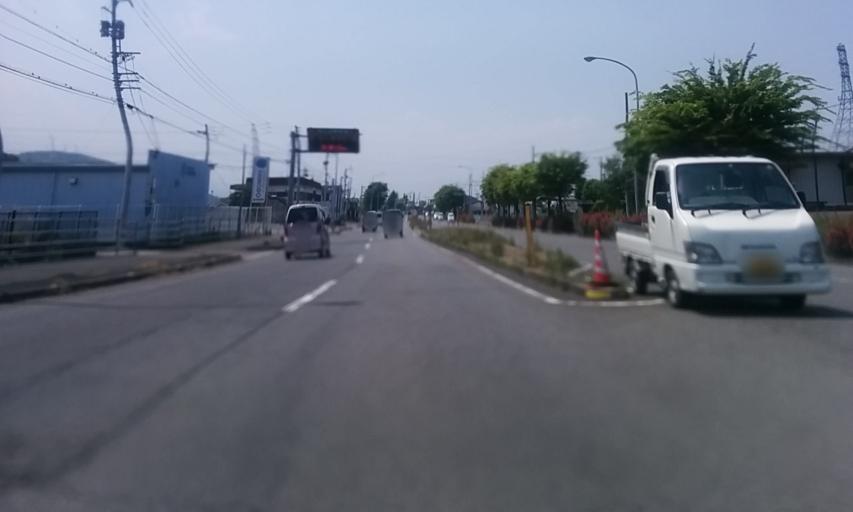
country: JP
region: Ehime
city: Saijo
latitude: 33.9203
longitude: 133.2439
